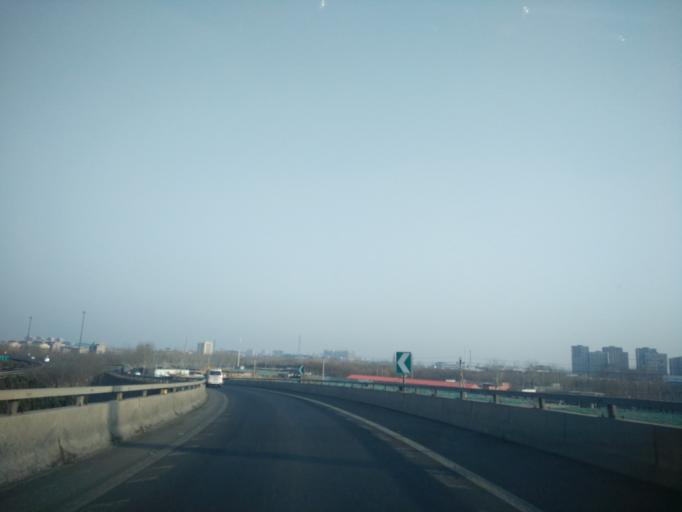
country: CN
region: Beijing
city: Jiugong
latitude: 39.8173
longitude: 116.4972
